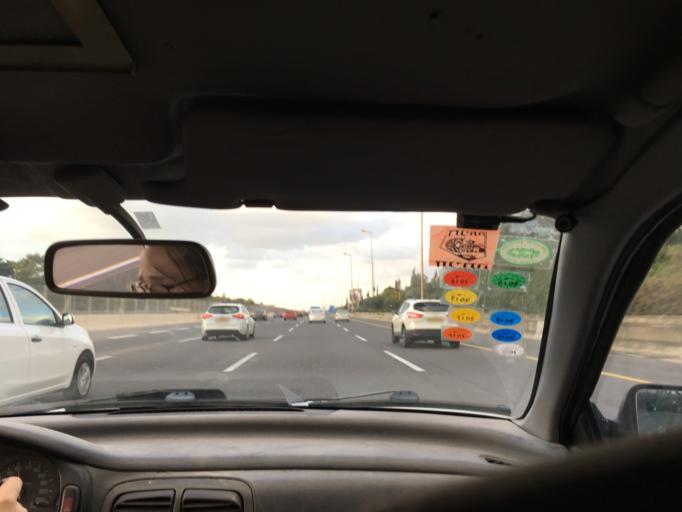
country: IL
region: Tel Aviv
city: Ramat Gan
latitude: 32.1176
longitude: 34.8108
